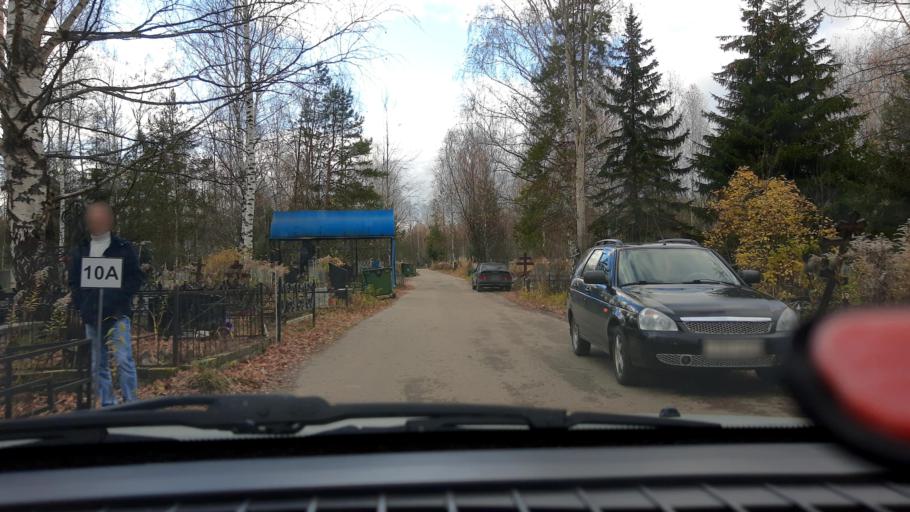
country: RU
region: Nizjnij Novgorod
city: Gorbatovka
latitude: 56.3606
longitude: 43.7838
